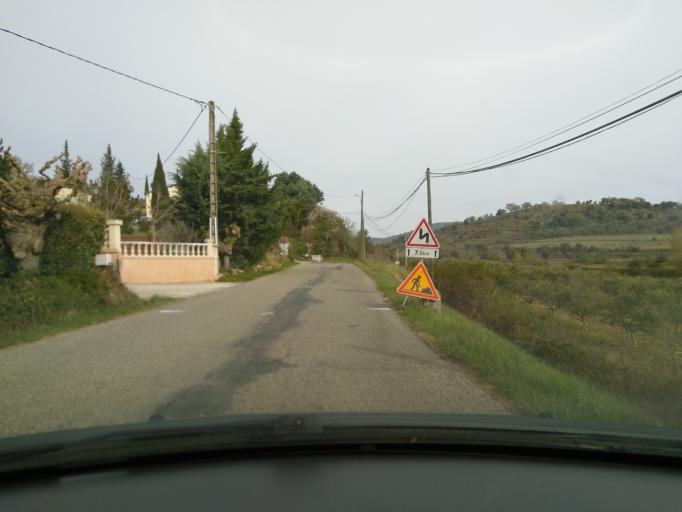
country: FR
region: Rhone-Alpes
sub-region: Departement de l'Ardeche
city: Ruoms
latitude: 44.4576
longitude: 4.4144
